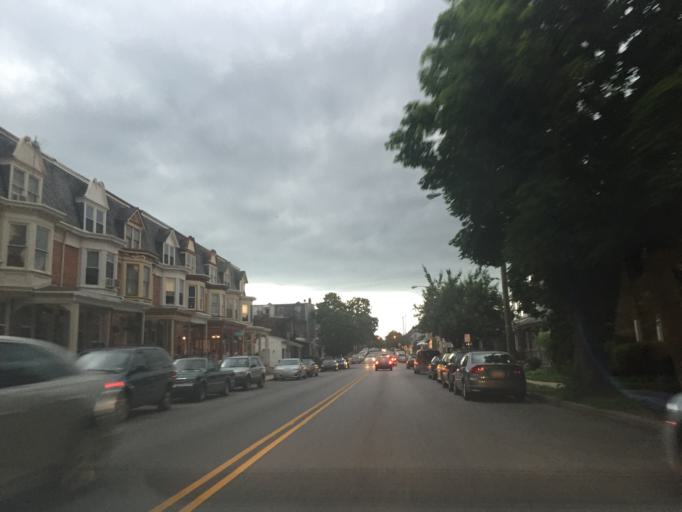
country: US
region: Pennsylvania
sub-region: York County
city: West York
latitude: 39.9663
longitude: -76.7457
